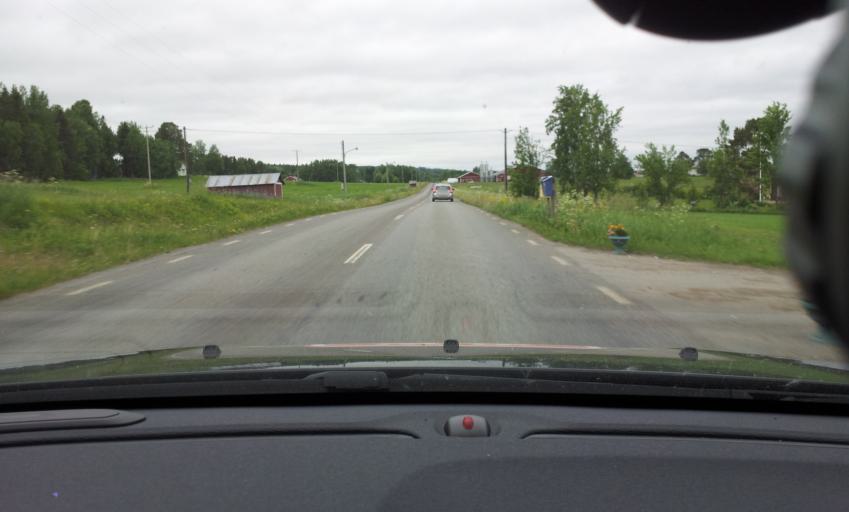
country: SE
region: Jaemtland
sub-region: Krokoms Kommun
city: Krokom
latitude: 63.1626
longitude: 14.1257
